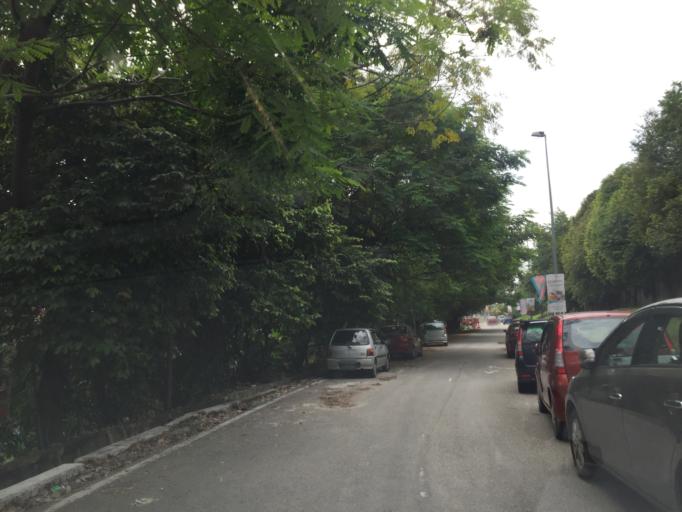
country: MY
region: Selangor
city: Klang
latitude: 3.0393
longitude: 101.4450
